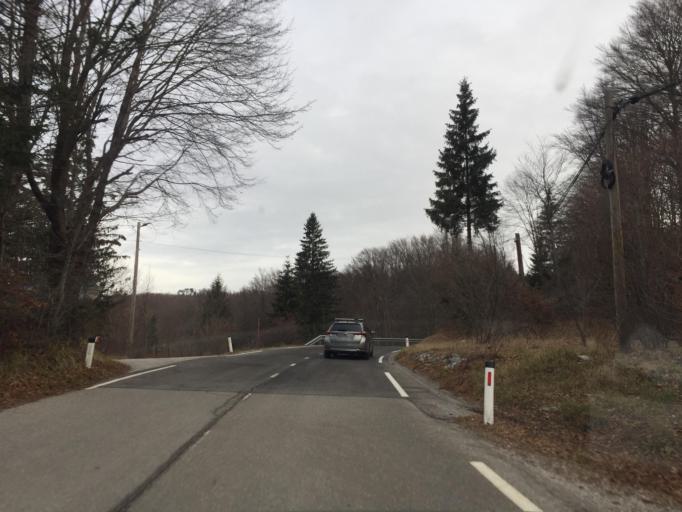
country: SI
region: Nova Gorica
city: Sempas
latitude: 45.9805
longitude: 13.7524
